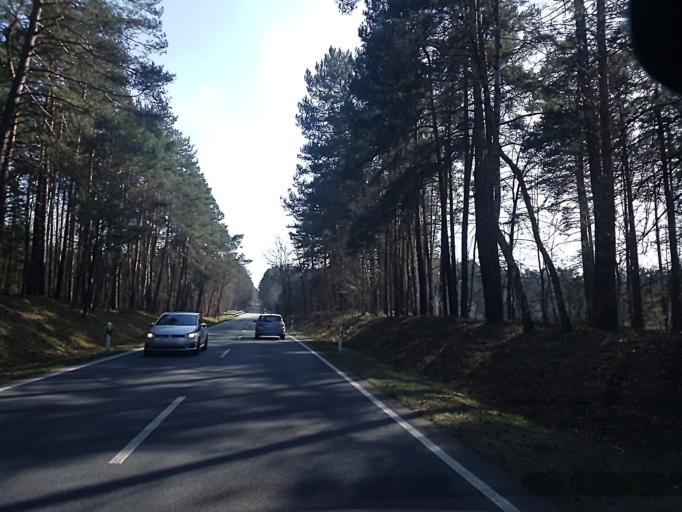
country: DE
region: Brandenburg
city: Calau
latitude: 51.7127
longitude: 13.9207
